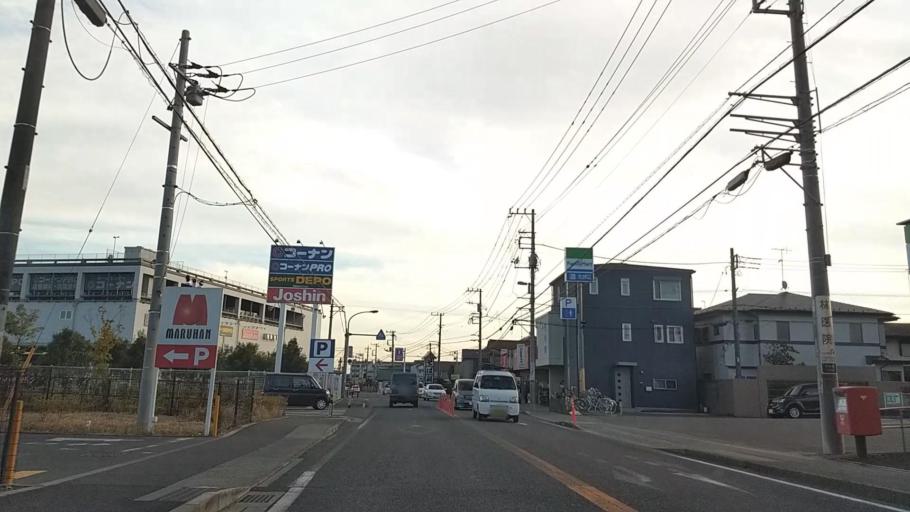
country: JP
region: Kanagawa
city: Atsugi
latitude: 35.4753
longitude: 139.3444
